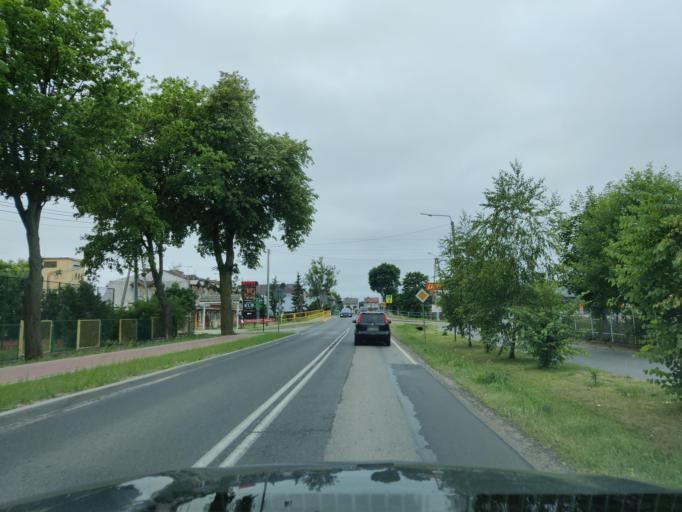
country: PL
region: Masovian Voivodeship
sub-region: Powiat ostrolecki
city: Myszyniec
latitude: 53.3875
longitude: 21.3414
